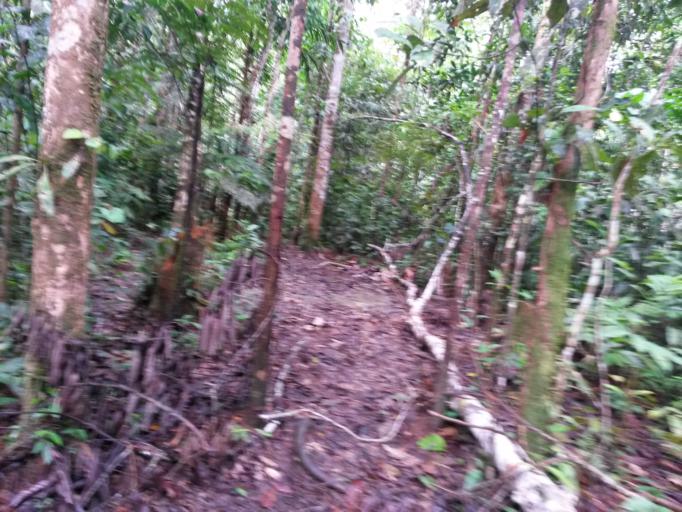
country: CO
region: Putumayo
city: Puerto Guzman
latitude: 1.0103
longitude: -76.3469
